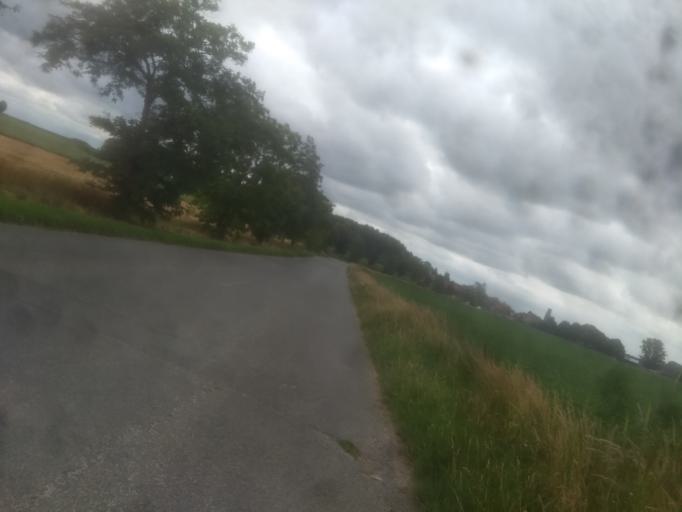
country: FR
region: Nord-Pas-de-Calais
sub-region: Departement du Pas-de-Calais
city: Thelus
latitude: 50.3322
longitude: 2.7934
